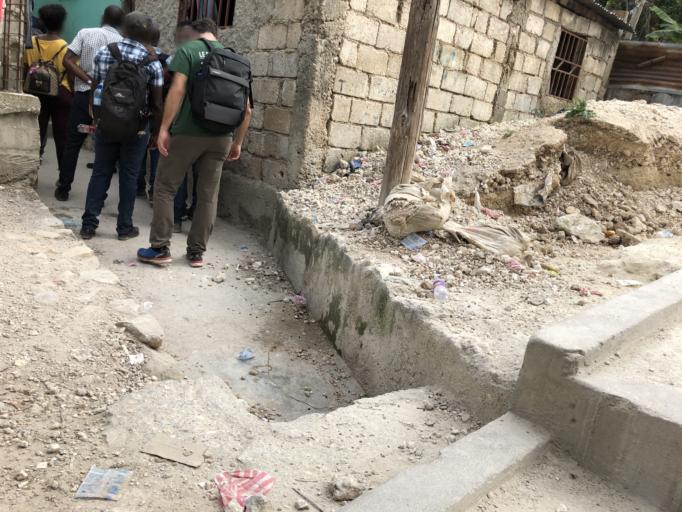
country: HT
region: Ouest
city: Port-au-Prince
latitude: 18.5239
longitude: -72.3188
